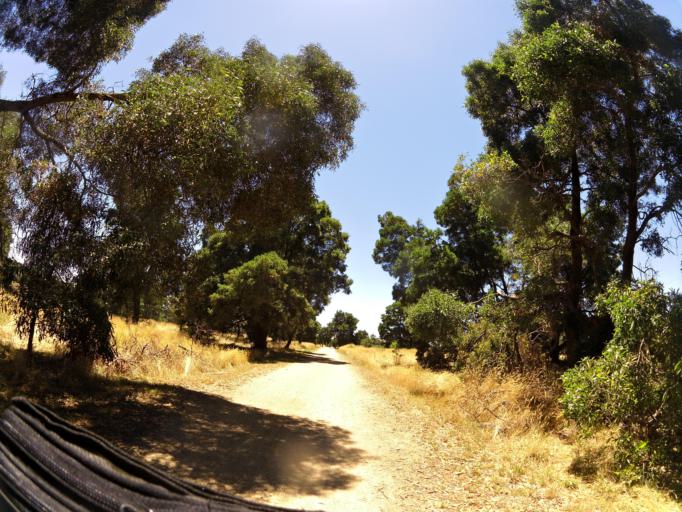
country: AU
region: Victoria
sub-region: Ballarat North
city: Delacombe
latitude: -37.6216
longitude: 143.7053
